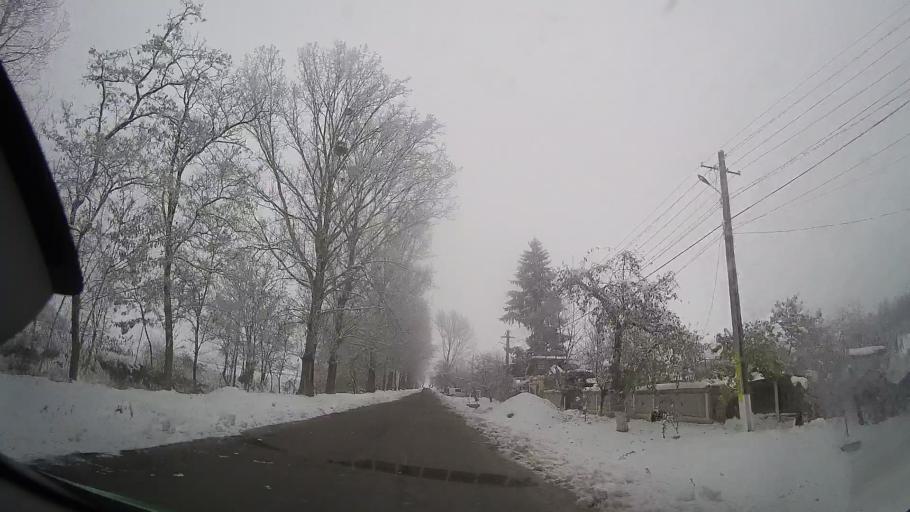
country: RO
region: Neamt
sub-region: Comuna Valea Ursului
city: Chilii
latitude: 46.8503
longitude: 27.0415
